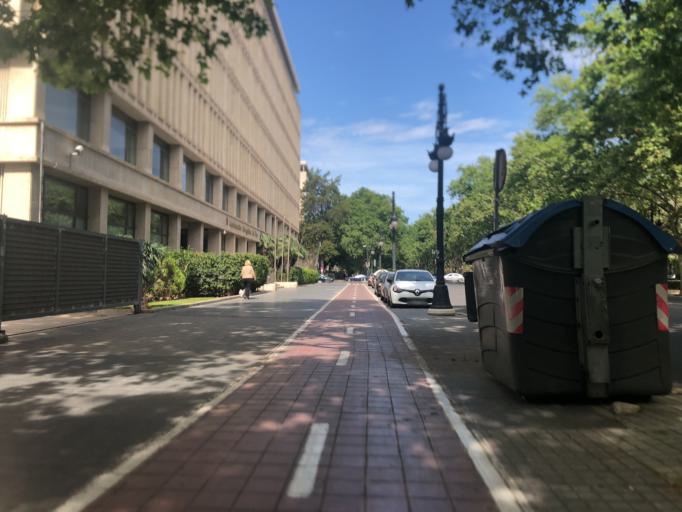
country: ES
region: Valencia
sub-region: Provincia de Valencia
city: Valencia
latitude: 39.4763
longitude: -0.3572
